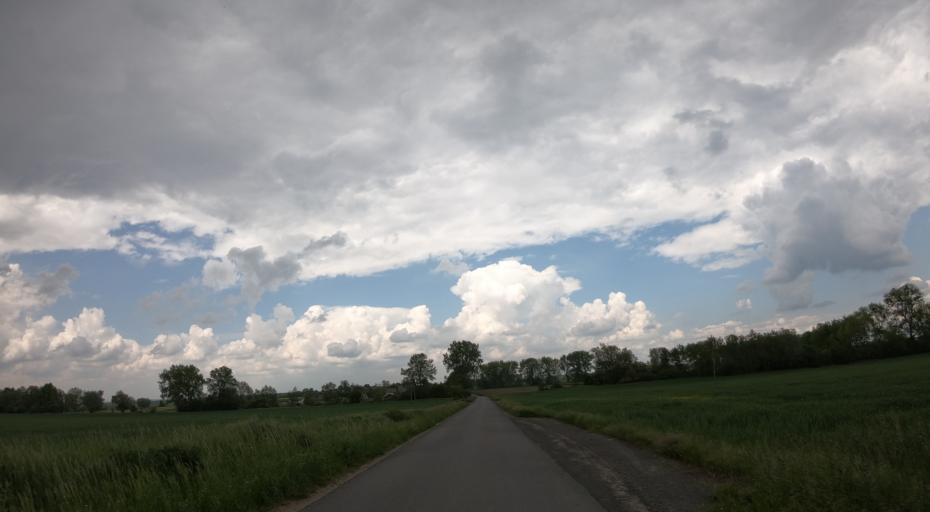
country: PL
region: West Pomeranian Voivodeship
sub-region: Powiat pyrzycki
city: Bielice
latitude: 53.2220
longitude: 14.7668
